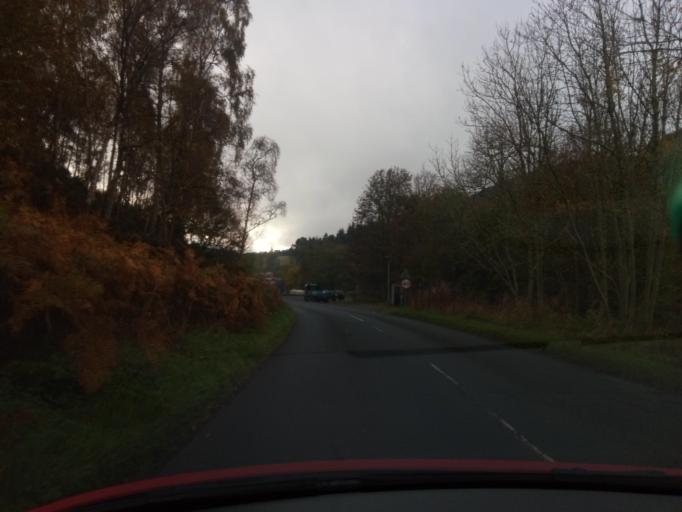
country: GB
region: Scotland
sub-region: The Scottish Borders
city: Selkirk
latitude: 55.6063
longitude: -2.8767
